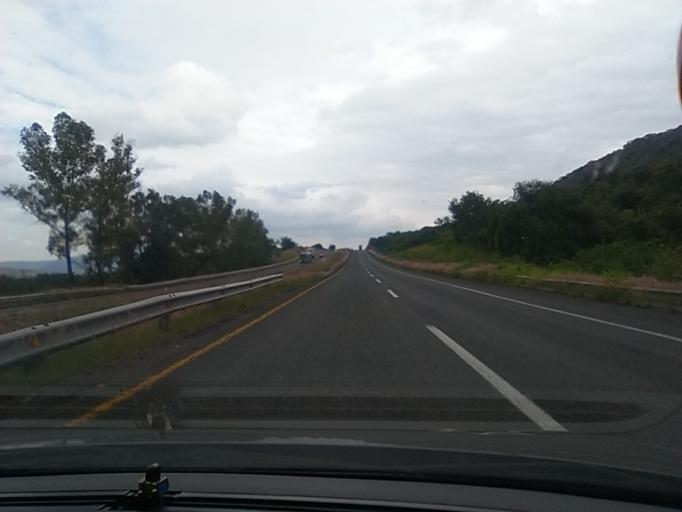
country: MX
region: Jalisco
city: Ocotlan
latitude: 20.4195
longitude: -102.7598
